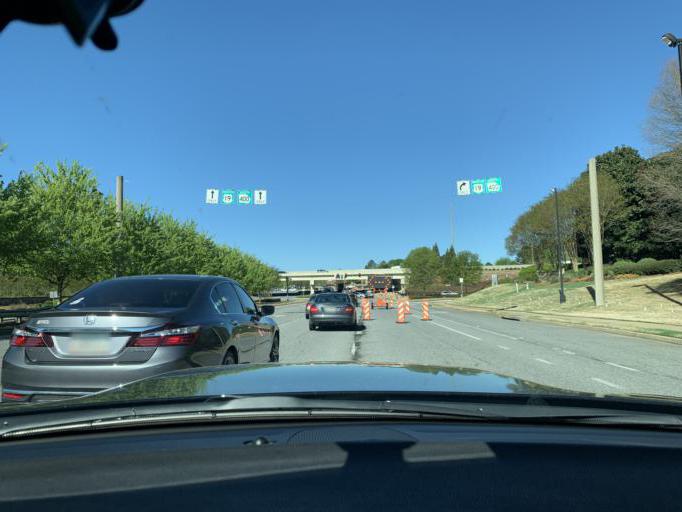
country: US
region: Georgia
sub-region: Fulton County
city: Alpharetta
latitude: 34.0885
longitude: -84.2594
